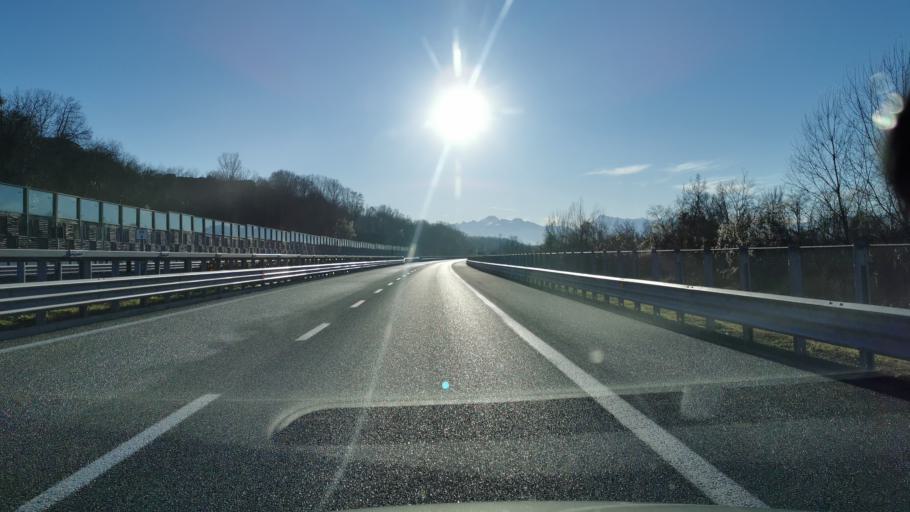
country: IT
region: Piedmont
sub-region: Provincia di Cuneo
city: Montanera
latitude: 44.4627
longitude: 7.6621
